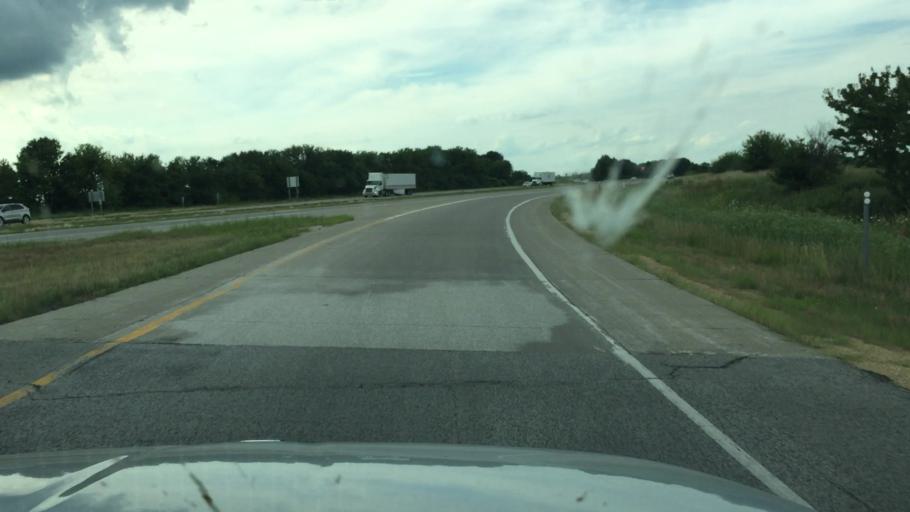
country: US
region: Iowa
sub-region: Scott County
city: Blue Grass
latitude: 41.5412
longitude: -90.6772
